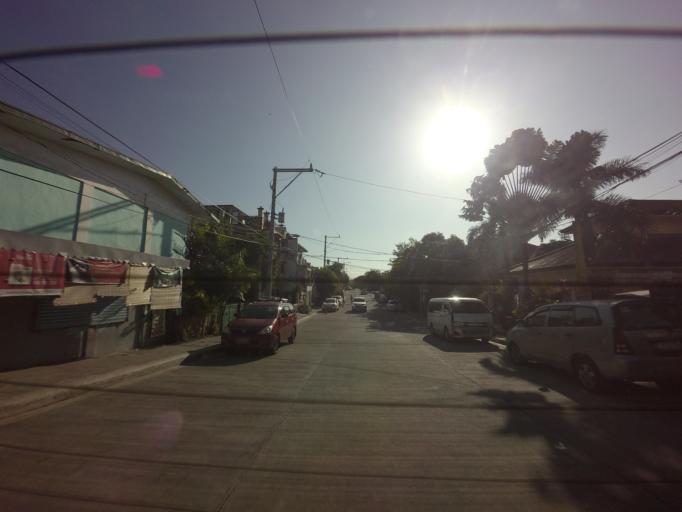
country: PH
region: Metro Manila
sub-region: Makati City
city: Makati City
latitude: 14.5304
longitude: 121.0360
